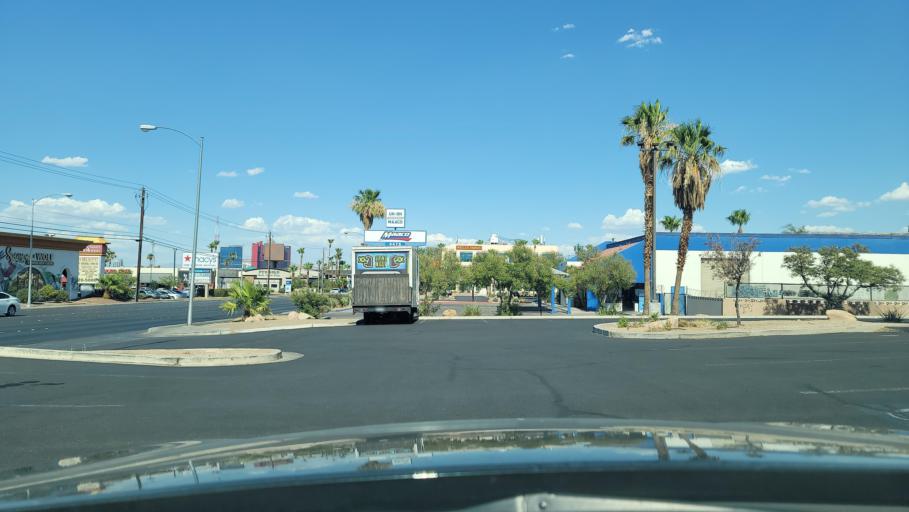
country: US
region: Nevada
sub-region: Clark County
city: Spring Valley
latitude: 36.1261
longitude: -115.2020
